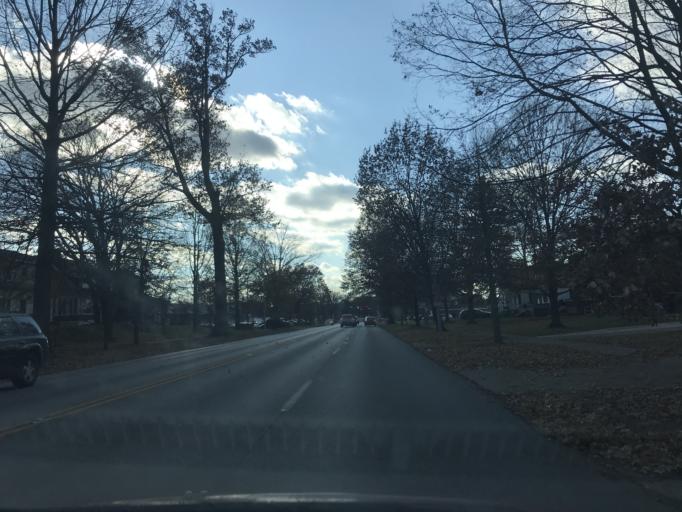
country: US
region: Kentucky
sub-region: Jefferson County
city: Audubon Park
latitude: 38.2160
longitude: -85.7406
